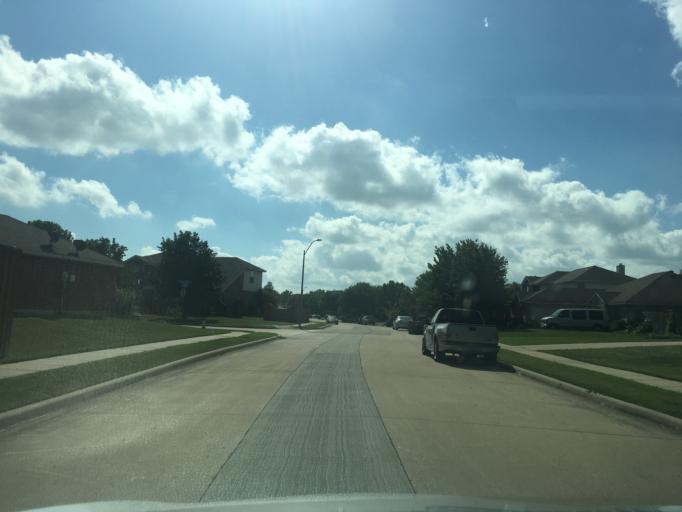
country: US
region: Texas
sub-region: Dallas County
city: Sachse
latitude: 32.9570
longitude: -96.5901
